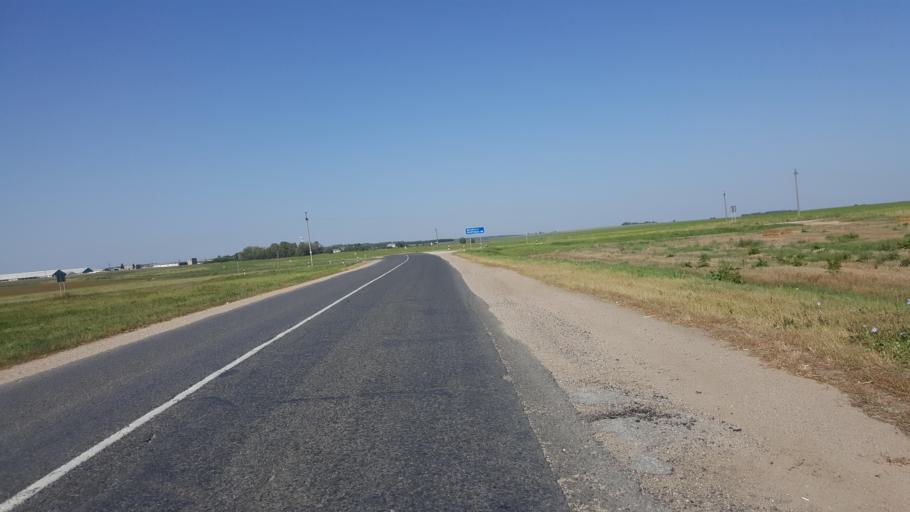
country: BY
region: Brest
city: Kamyanyets
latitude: 52.4172
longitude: 23.6207
